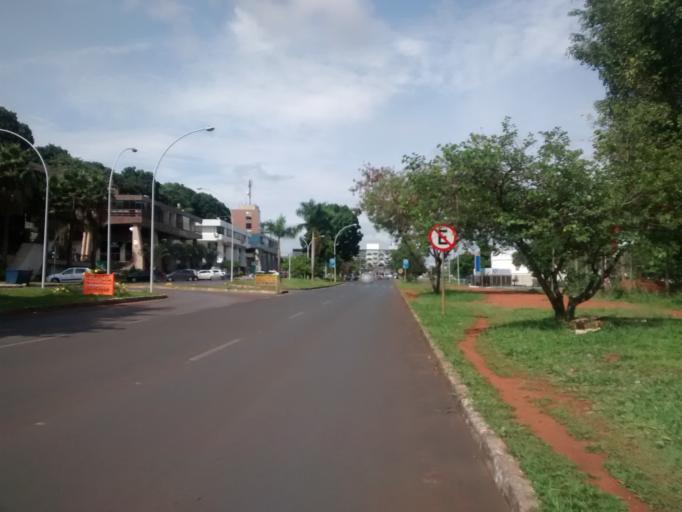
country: BR
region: Federal District
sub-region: Brasilia
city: Brasilia
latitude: -15.7375
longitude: -47.8965
